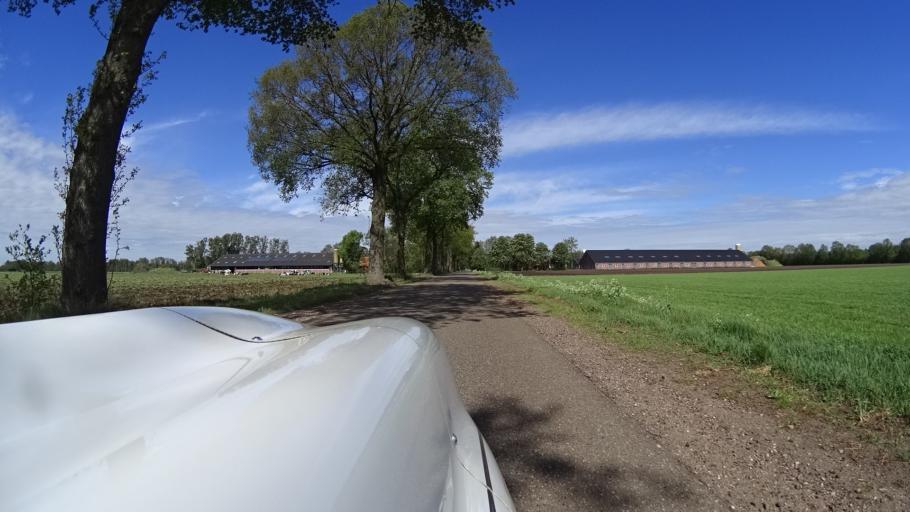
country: NL
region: North Brabant
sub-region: Gemeente Mill en Sint Hubert
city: Wilbertoord
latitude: 51.6036
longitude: 5.8012
